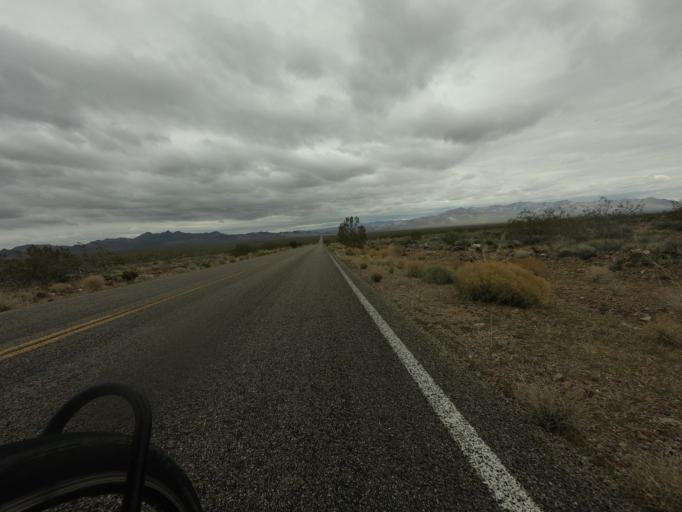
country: US
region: Nevada
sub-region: Nye County
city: Beatty
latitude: 36.8175
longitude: -116.8992
